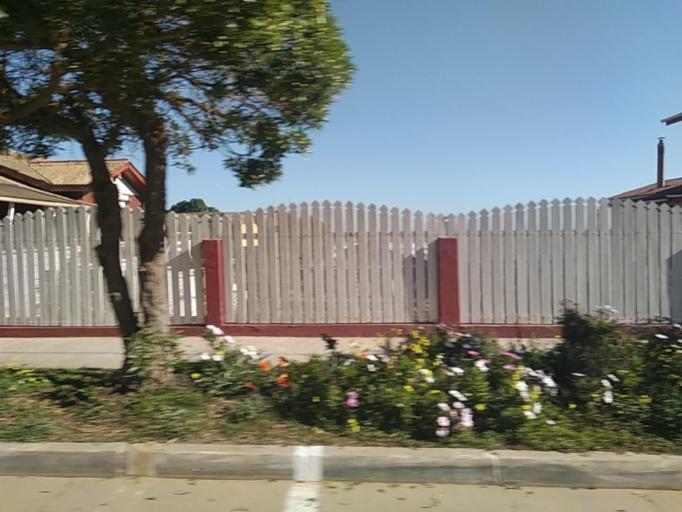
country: CL
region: Valparaiso
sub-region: San Antonio Province
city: El Tabo
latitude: -33.4592
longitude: -71.6594
